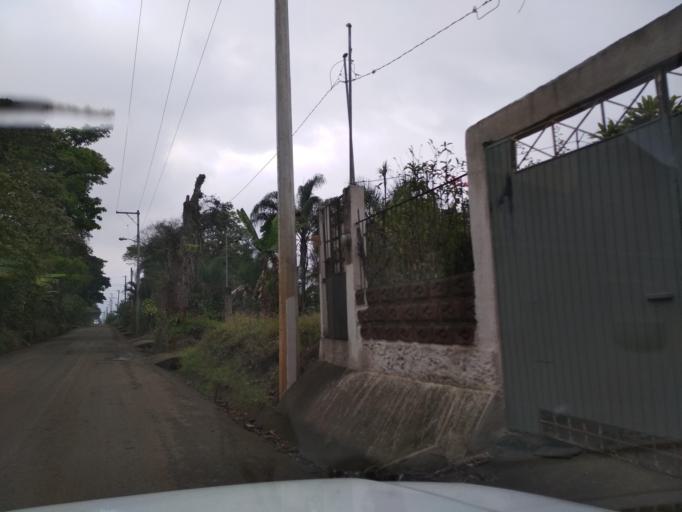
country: MX
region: Veracruz
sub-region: Cordoba
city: Veinte de Noviembre
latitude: 18.8622
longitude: -96.9655
